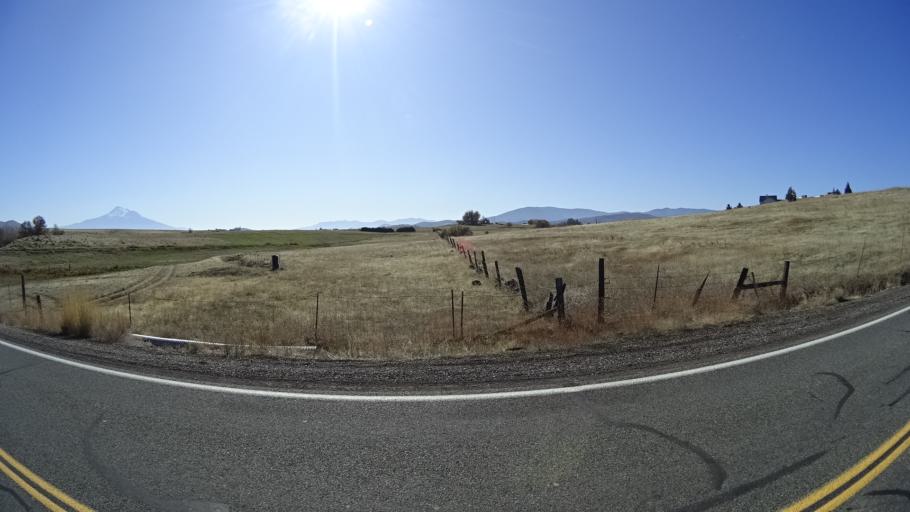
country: US
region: California
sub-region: Siskiyou County
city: Montague
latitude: 41.7456
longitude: -122.5784
